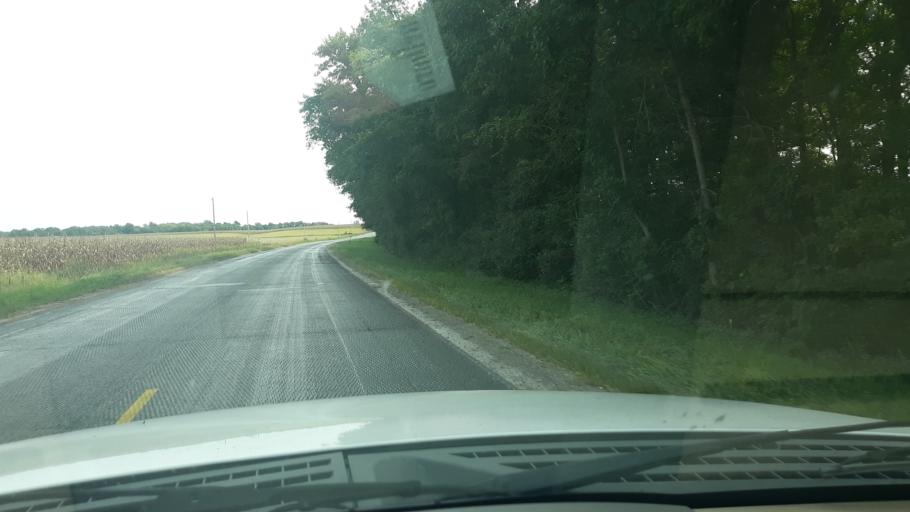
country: US
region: Illinois
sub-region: Edwards County
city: Grayville
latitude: 38.2928
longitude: -87.9710
